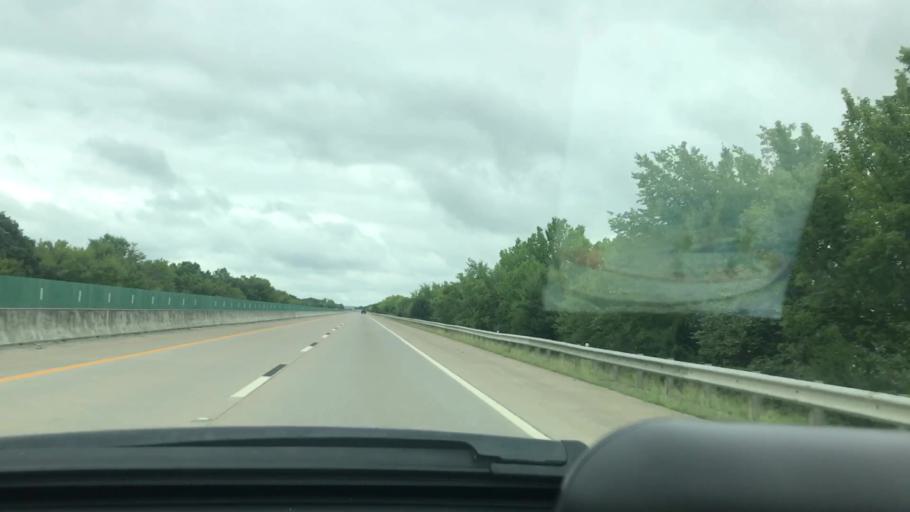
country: US
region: Oklahoma
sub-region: Pittsburg County
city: Krebs
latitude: 35.0200
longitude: -95.7168
